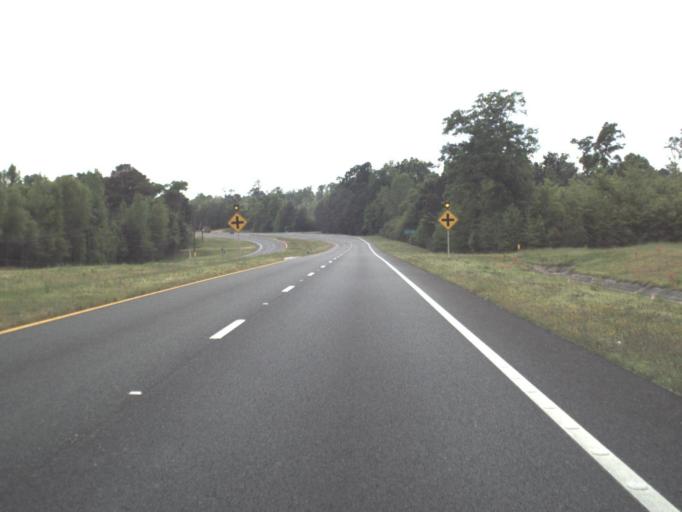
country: US
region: Florida
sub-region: Escambia County
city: Century
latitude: 30.9398
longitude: -87.2924
